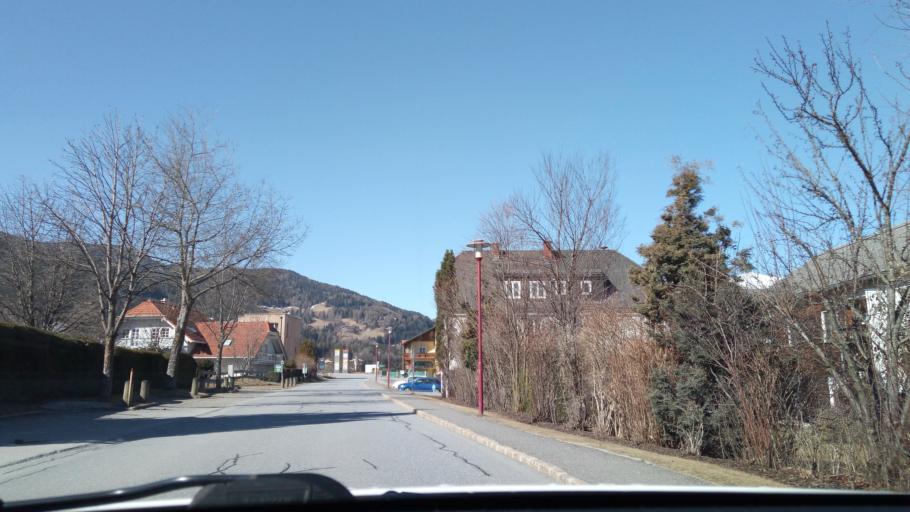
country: AT
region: Styria
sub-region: Politischer Bezirk Murau
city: Sankt Georgen ob Murau
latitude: 47.1021
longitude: 14.0945
